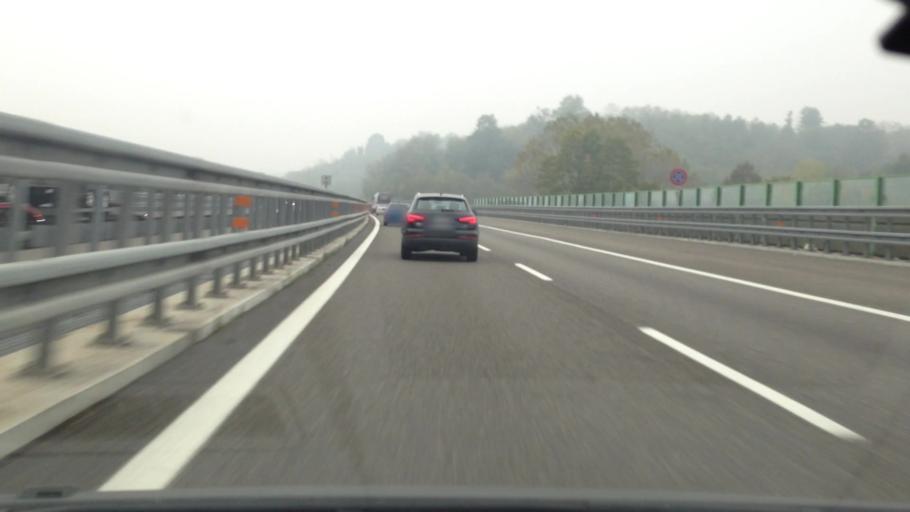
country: IT
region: Piedmont
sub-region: Provincia di Asti
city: Rocca d'Arazzo
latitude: 44.9110
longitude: 8.2914
